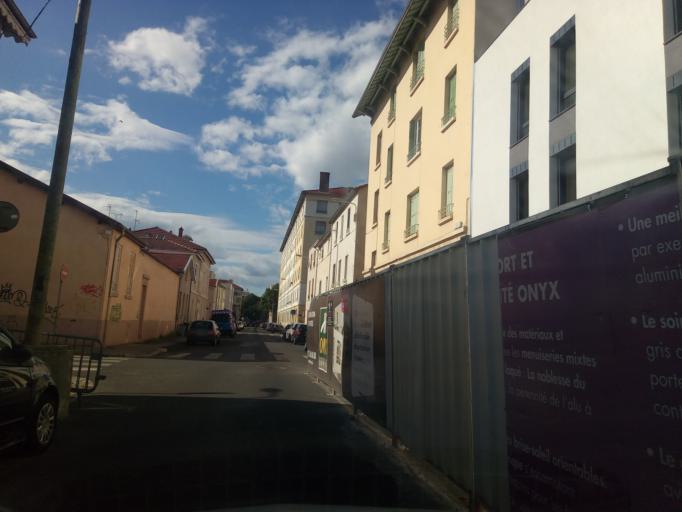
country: FR
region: Rhone-Alpes
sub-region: Departement du Rhone
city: Villeurbanne
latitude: 45.7516
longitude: 4.8871
